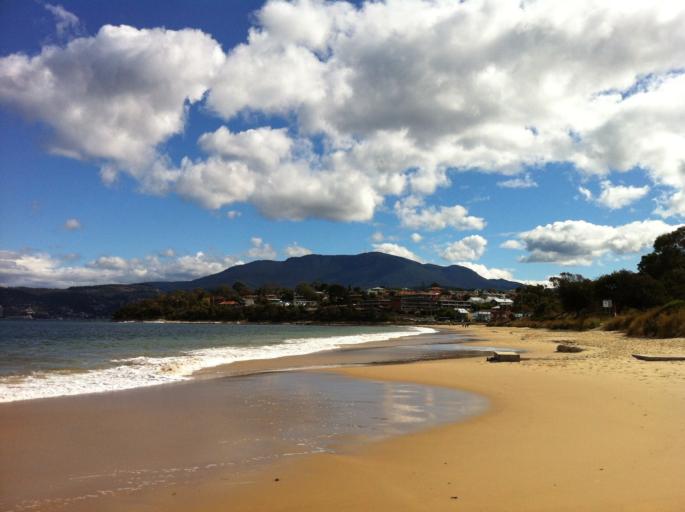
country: AU
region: Tasmania
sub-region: Clarence
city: Bellerive
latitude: -42.8789
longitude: 147.3757
